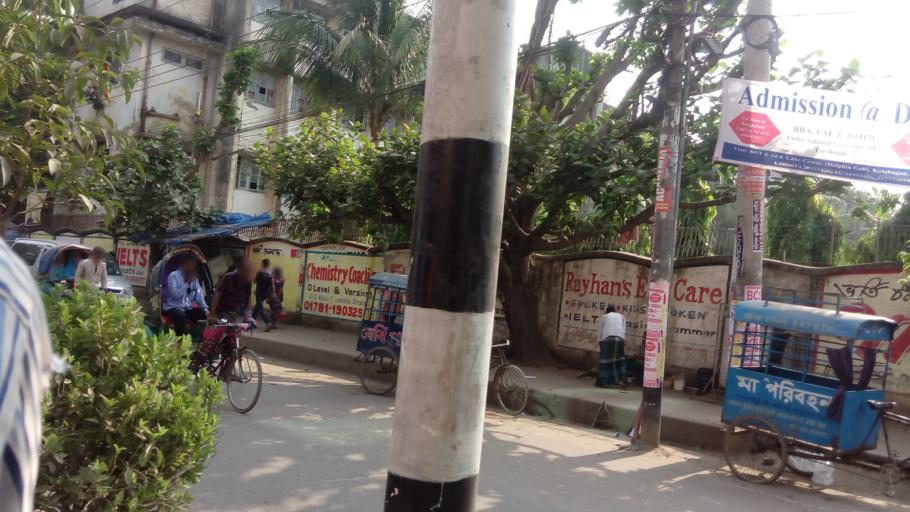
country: BD
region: Dhaka
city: Azimpur
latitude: 23.7545
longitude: 90.3647
